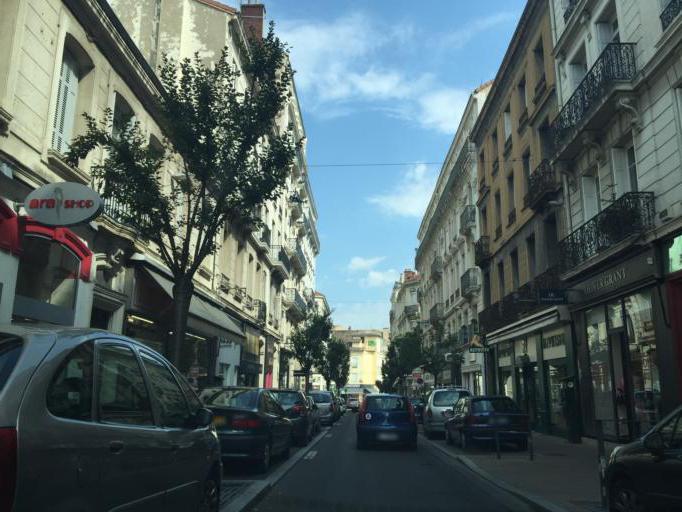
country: FR
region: Rhone-Alpes
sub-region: Departement de la Loire
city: Saint-Etienne
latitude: 45.4357
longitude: 4.3894
